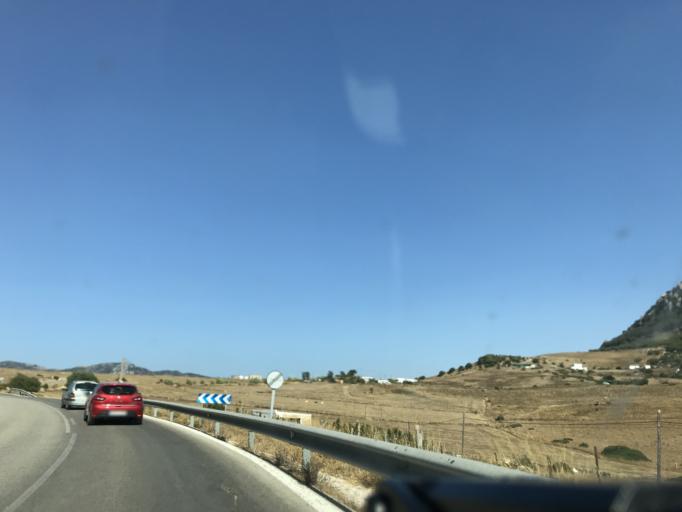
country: ES
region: Andalusia
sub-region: Provincia de Cadiz
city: Zahara de los Atunes
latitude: 36.1015
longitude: -5.7383
